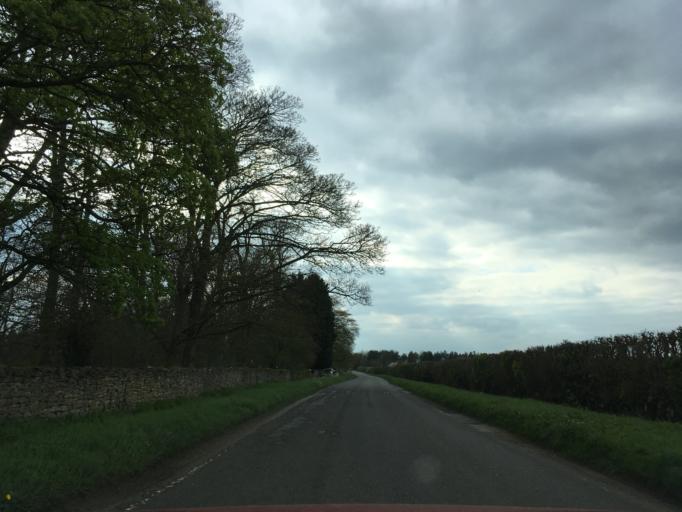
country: GB
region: England
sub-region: Oxfordshire
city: Kidlington
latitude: 51.8806
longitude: -1.2684
